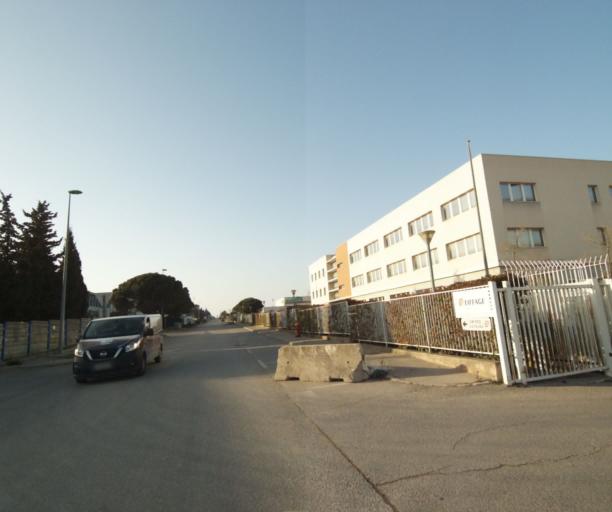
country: FR
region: Provence-Alpes-Cote d'Azur
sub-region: Departement des Bouches-du-Rhone
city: Saint-Victoret
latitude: 43.4264
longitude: 5.2439
